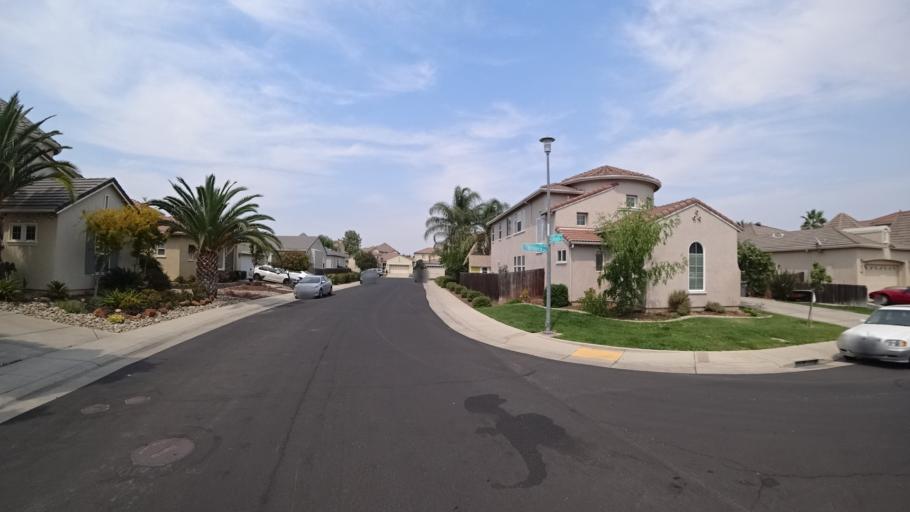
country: US
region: California
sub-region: Sacramento County
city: Laguna
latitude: 38.3870
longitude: -121.4253
